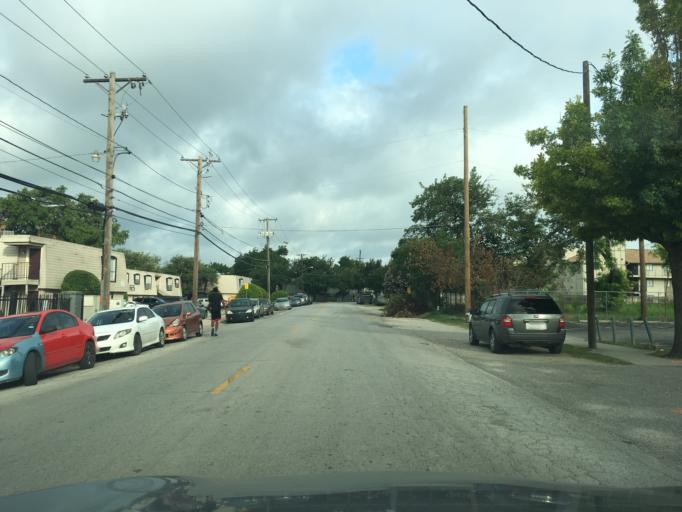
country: US
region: Texas
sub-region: Dallas County
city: University Park
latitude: 32.8665
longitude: -96.7532
